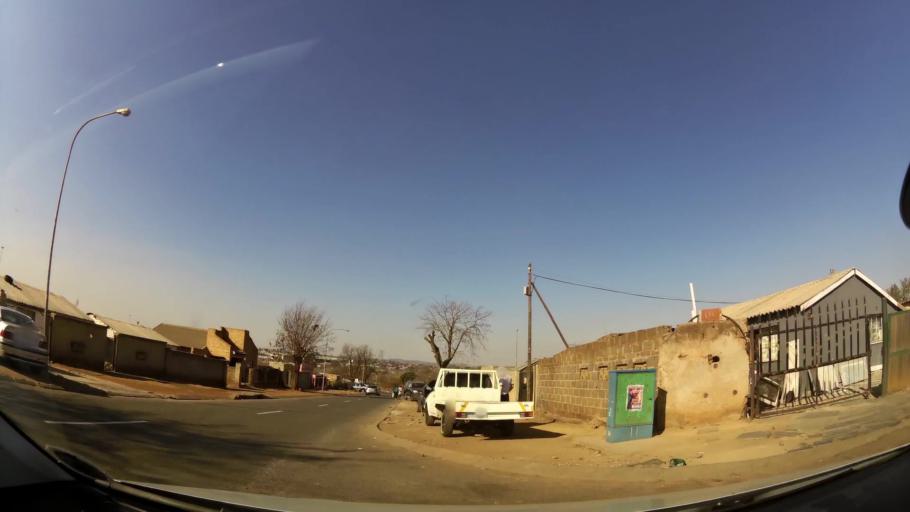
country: ZA
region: Gauteng
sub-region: City of Johannesburg Metropolitan Municipality
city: Soweto
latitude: -26.2802
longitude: 27.8740
